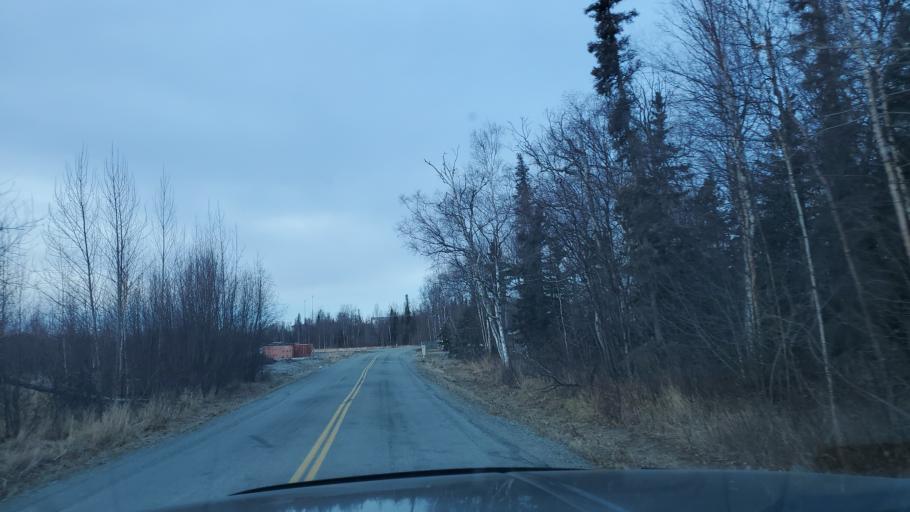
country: US
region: Alaska
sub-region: Matanuska-Susitna Borough
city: Lakes
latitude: 61.5730
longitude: -149.3413
